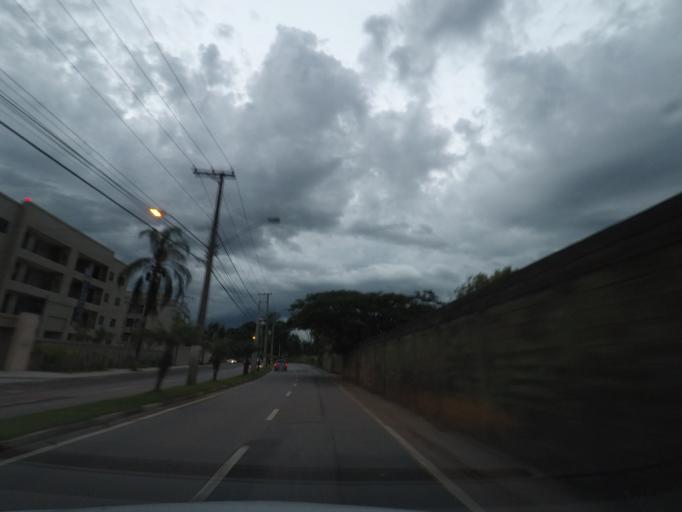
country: BR
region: Sao Paulo
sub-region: Vinhedo
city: Vinhedo
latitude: -23.0320
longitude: -46.9921
